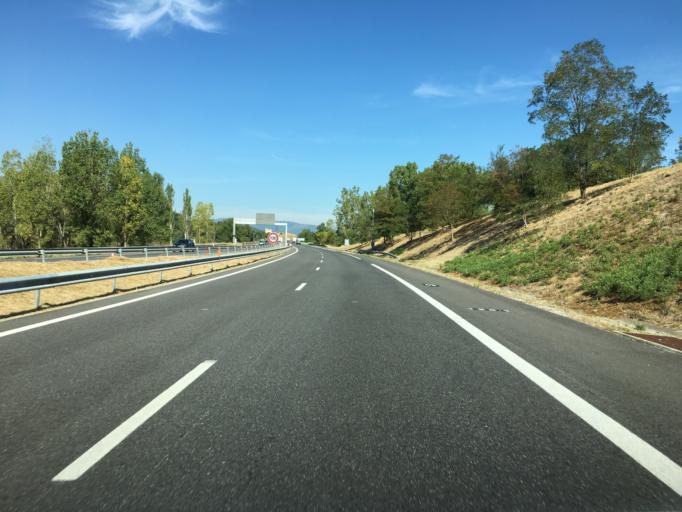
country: FR
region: Provence-Alpes-Cote d'Azur
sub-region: Departement des Alpes-de-Haute-Provence
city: Sisteron
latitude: 44.2025
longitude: 5.9457
